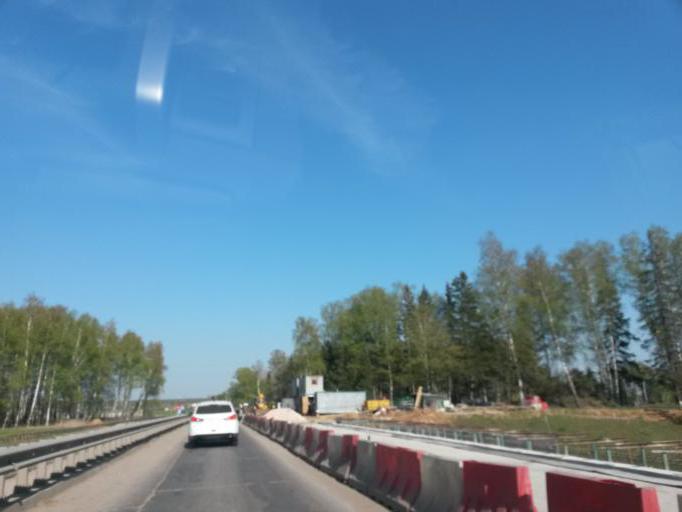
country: RU
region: Moskovskaya
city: Lyubuchany
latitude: 55.2447
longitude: 37.5279
